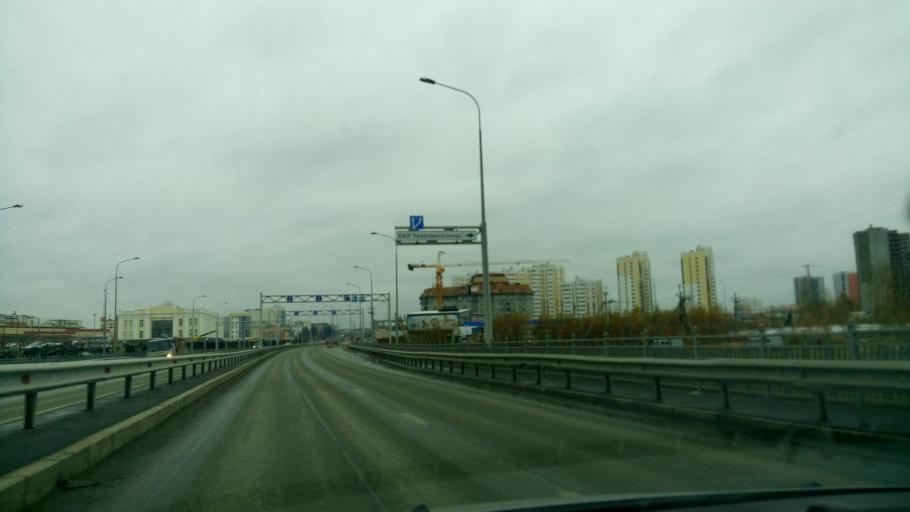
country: RU
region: Sverdlovsk
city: Verkhnyaya Pyshma
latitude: 56.9615
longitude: 60.5862
